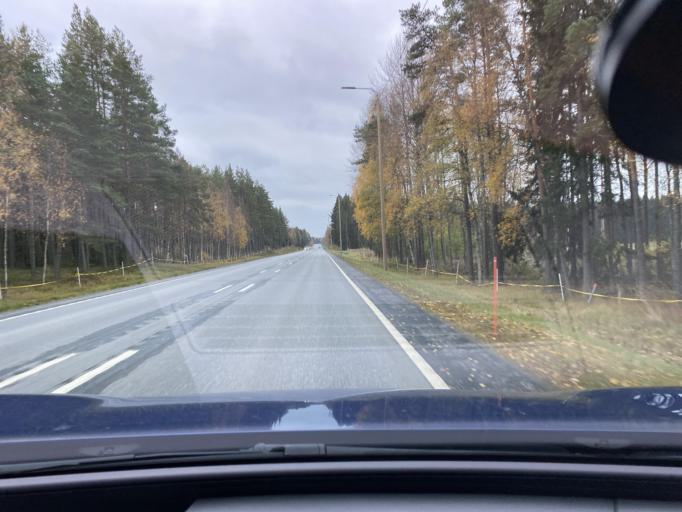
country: FI
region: Varsinais-Suomi
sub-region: Vakka-Suomi
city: Laitila
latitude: 60.9498
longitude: 21.5987
